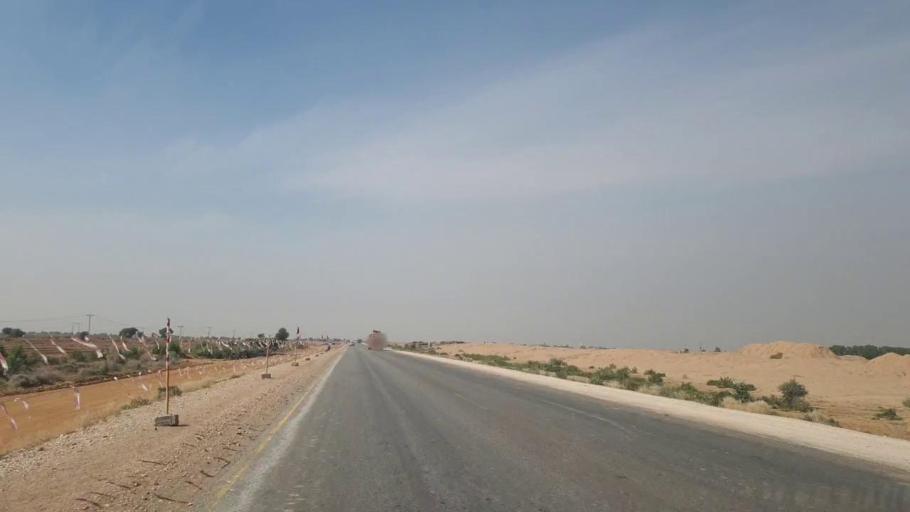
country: PK
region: Sindh
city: Sann
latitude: 26.0189
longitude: 68.1375
